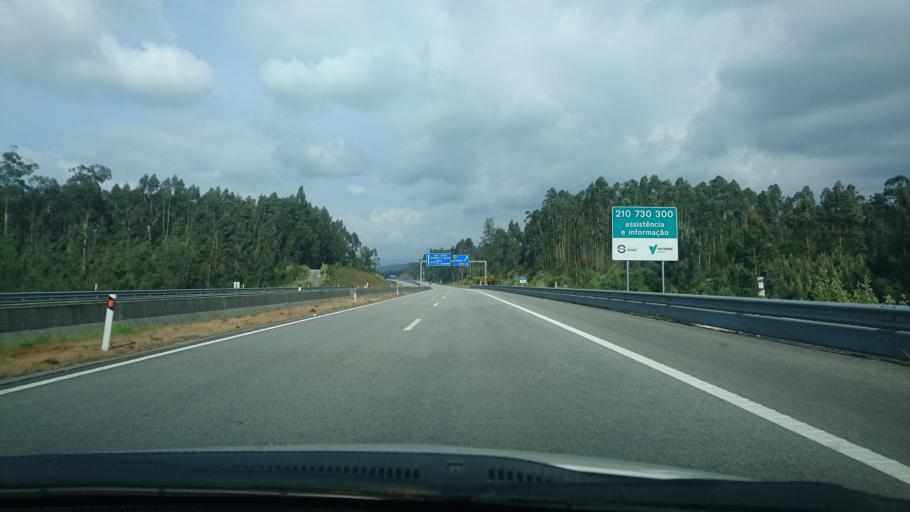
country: PT
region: Porto
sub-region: Vila Nova de Gaia
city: Sandim
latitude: 41.0220
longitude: -8.5156
